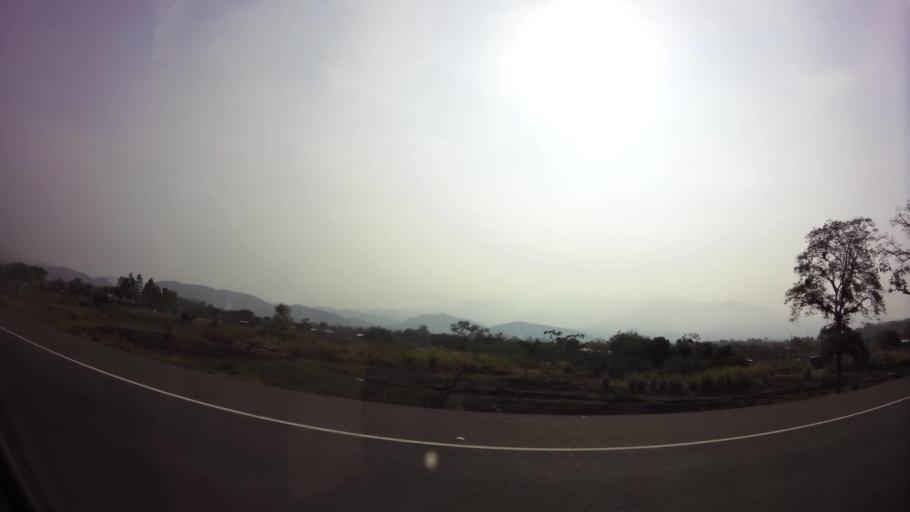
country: HN
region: Comayagua
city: Comayagua
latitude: 14.4578
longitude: -87.6664
